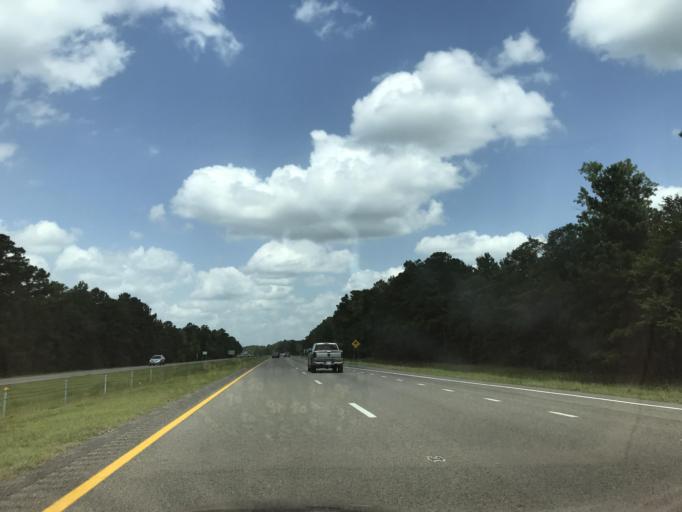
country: US
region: North Carolina
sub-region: Pender County
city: Burgaw
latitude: 34.5797
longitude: -77.9033
